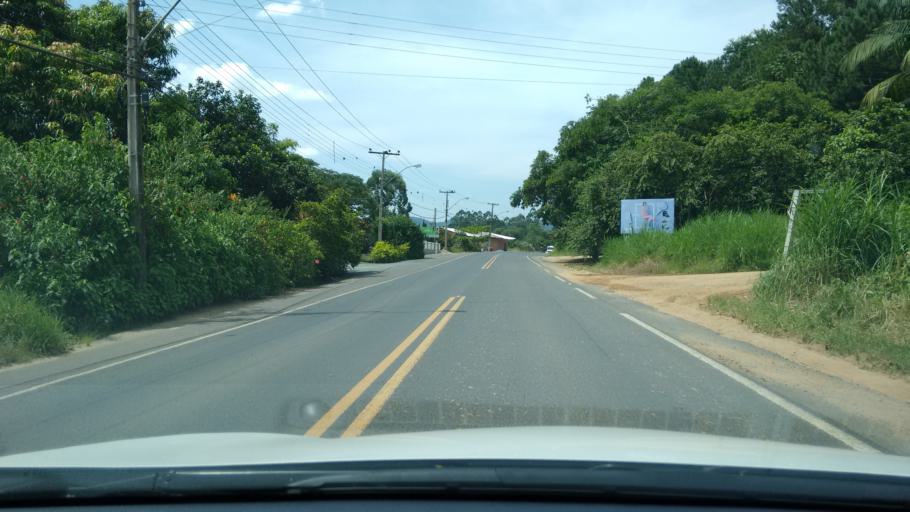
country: BR
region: Santa Catarina
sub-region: Timbo
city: Timbo
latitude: -26.8275
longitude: -49.2959
